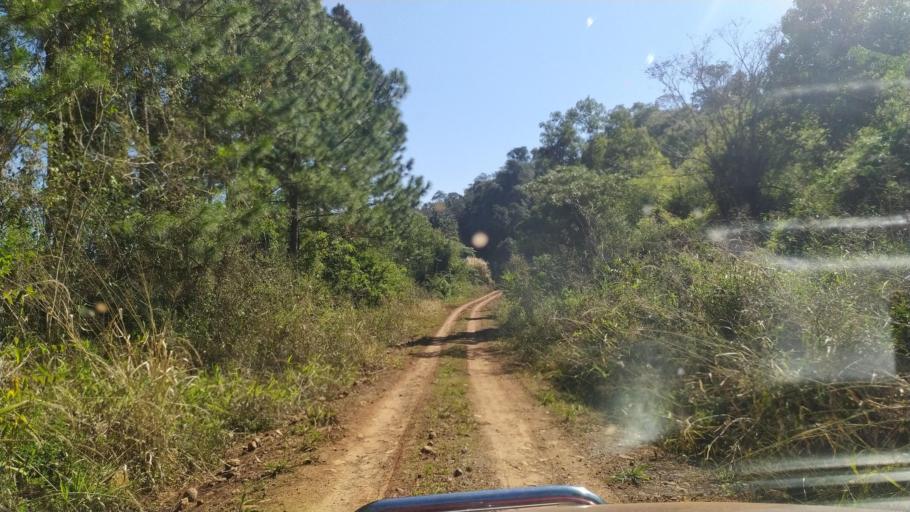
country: AR
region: Misiones
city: El Alcazar
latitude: -26.7567
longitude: -54.5942
